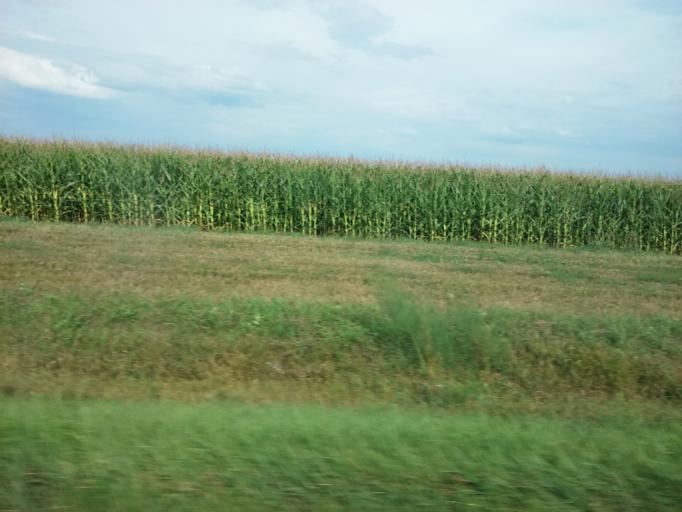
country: US
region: Ohio
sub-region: Hancock County
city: McComb
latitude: 41.2002
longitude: -83.7844
